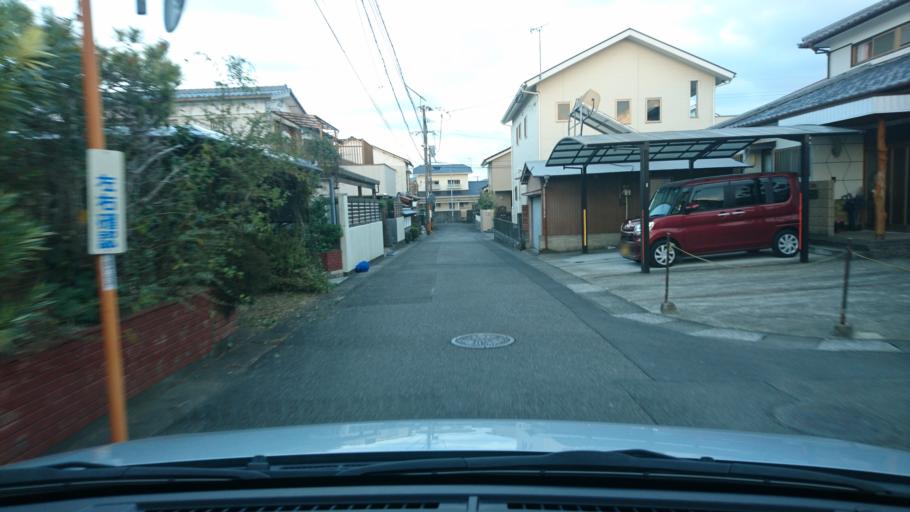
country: JP
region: Miyazaki
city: Miyazaki-shi
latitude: 31.8597
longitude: 131.4238
